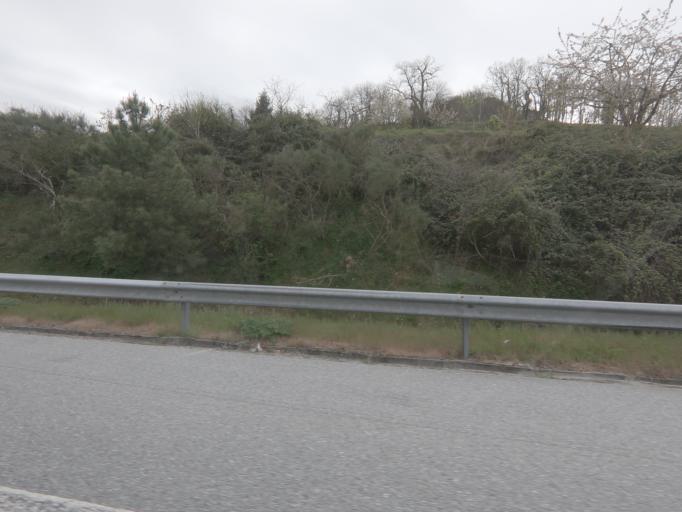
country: PT
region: Guarda
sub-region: Guarda
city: Sequeira
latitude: 40.5878
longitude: -7.2580
